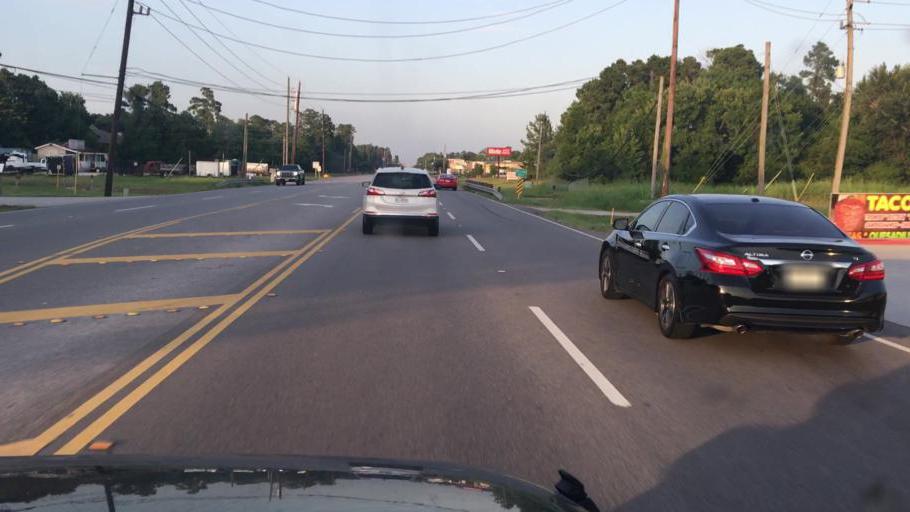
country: US
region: Texas
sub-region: Harris County
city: Atascocita
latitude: 29.9863
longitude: -95.1987
